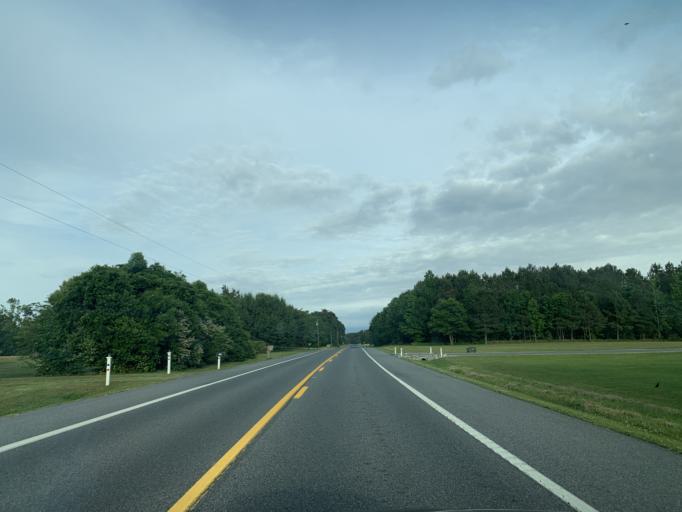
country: US
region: Maryland
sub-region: Worcester County
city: Pocomoke City
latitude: 38.0730
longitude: -75.4757
